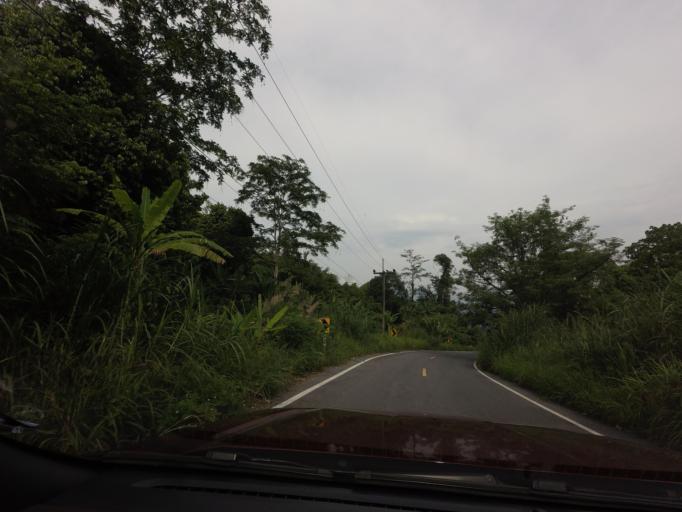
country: TH
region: Yala
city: Than To
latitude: 6.0728
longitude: 101.3469
